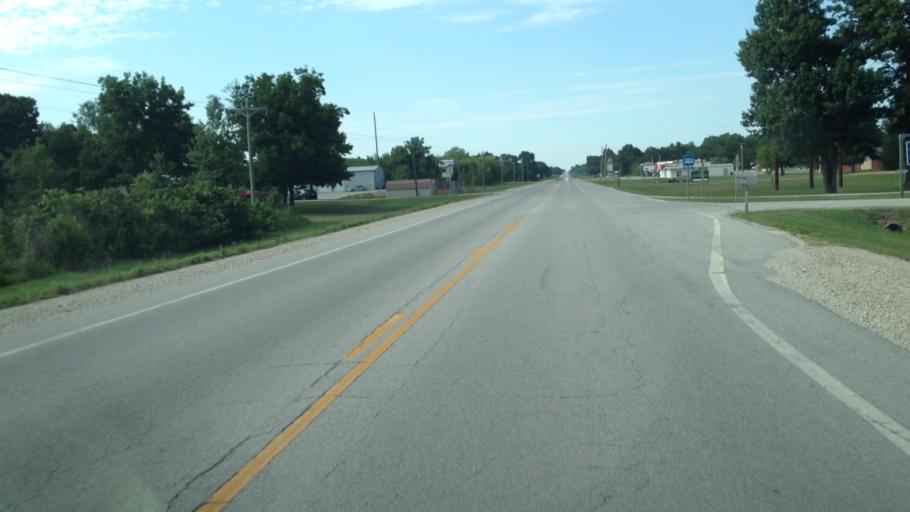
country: US
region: Kansas
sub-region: Neosho County
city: Erie
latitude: 37.5699
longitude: -95.2526
